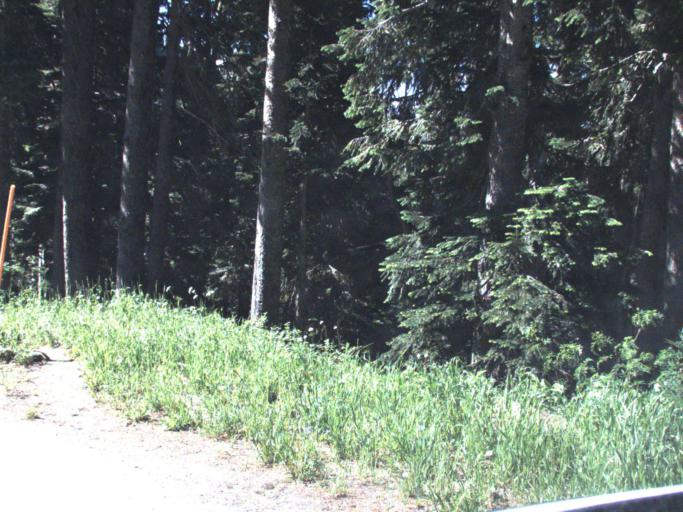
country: US
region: Washington
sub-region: King County
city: Enumclaw
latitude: 46.8711
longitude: -121.5153
